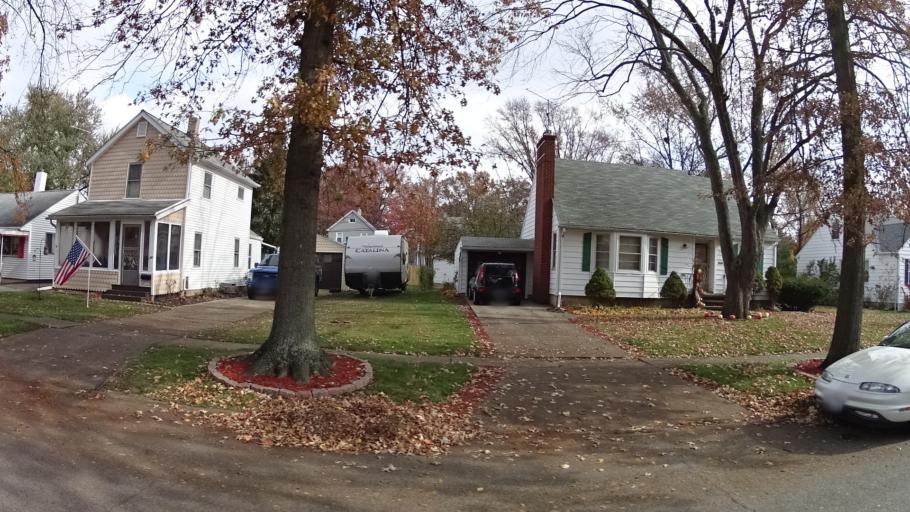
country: US
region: Ohio
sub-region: Lorain County
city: Elyria
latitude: 41.3808
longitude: -82.0837
